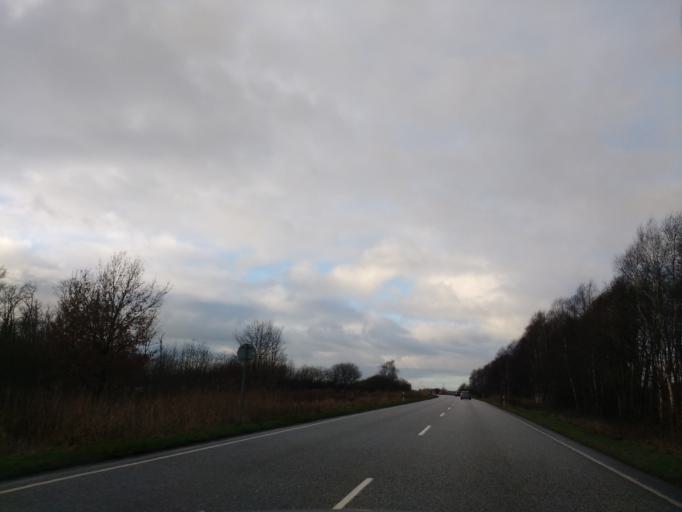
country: DE
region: Schleswig-Holstein
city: Heiligenstedten
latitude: 53.9376
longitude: 9.4660
